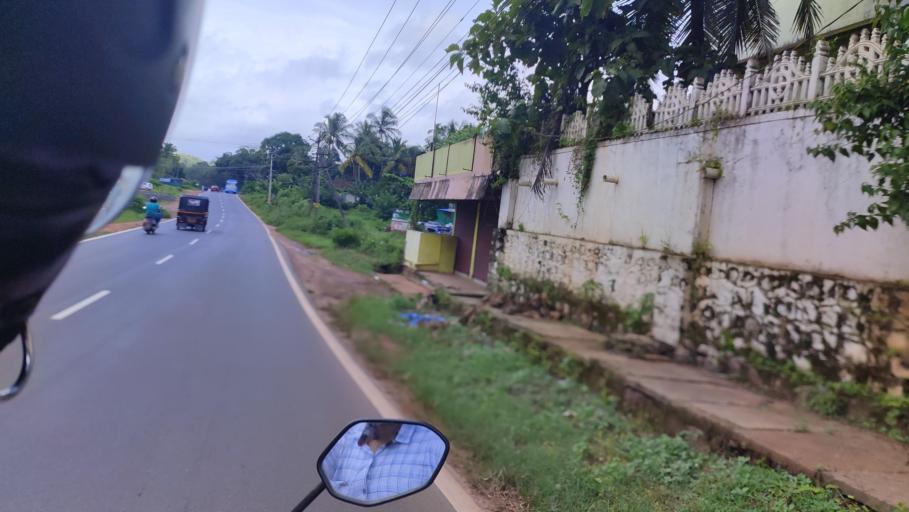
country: IN
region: Kerala
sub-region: Kasaragod District
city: Nileshwar
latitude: 12.2223
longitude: 75.1584
